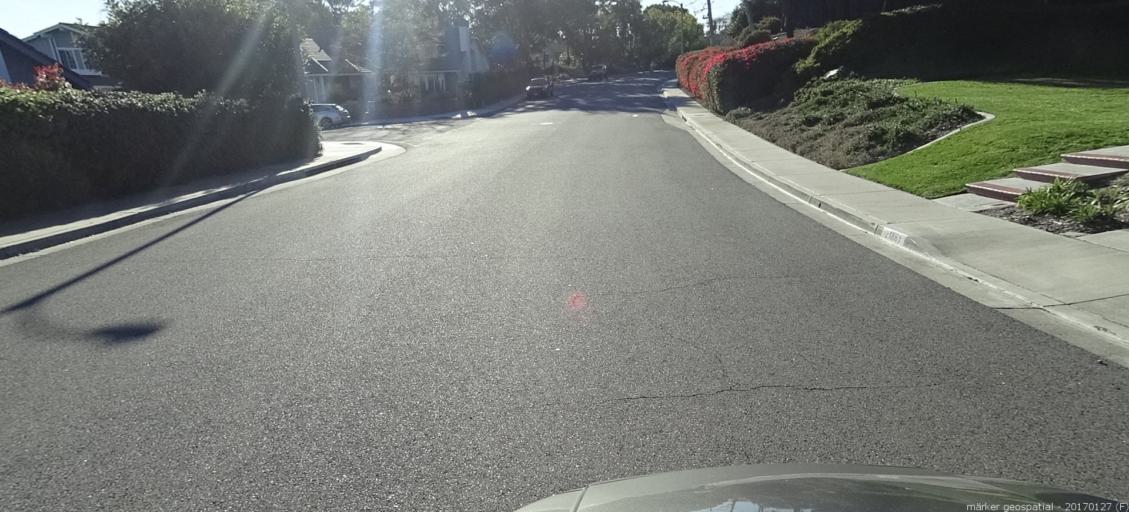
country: US
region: California
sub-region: Orange County
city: Lake Forest
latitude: 33.6454
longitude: -117.6671
